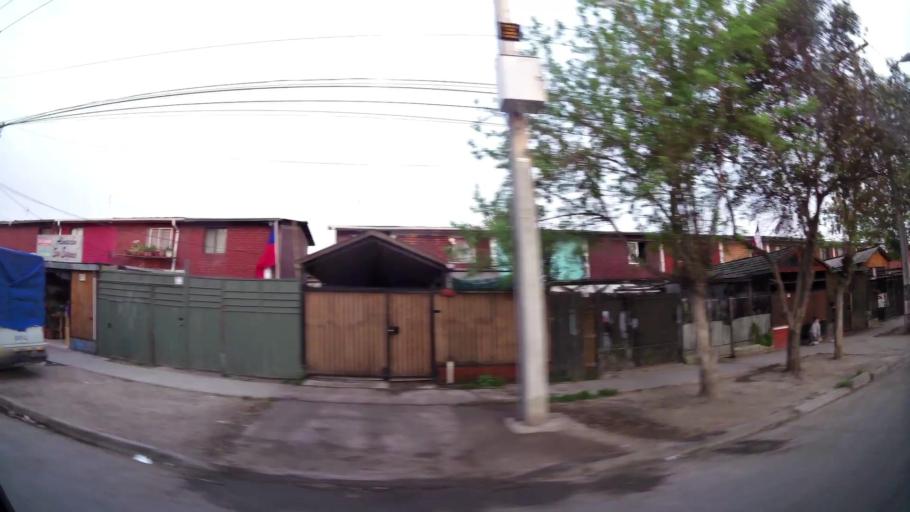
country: CL
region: Santiago Metropolitan
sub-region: Provincia de Santiago
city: Lo Prado
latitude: -33.5150
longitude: -70.7853
